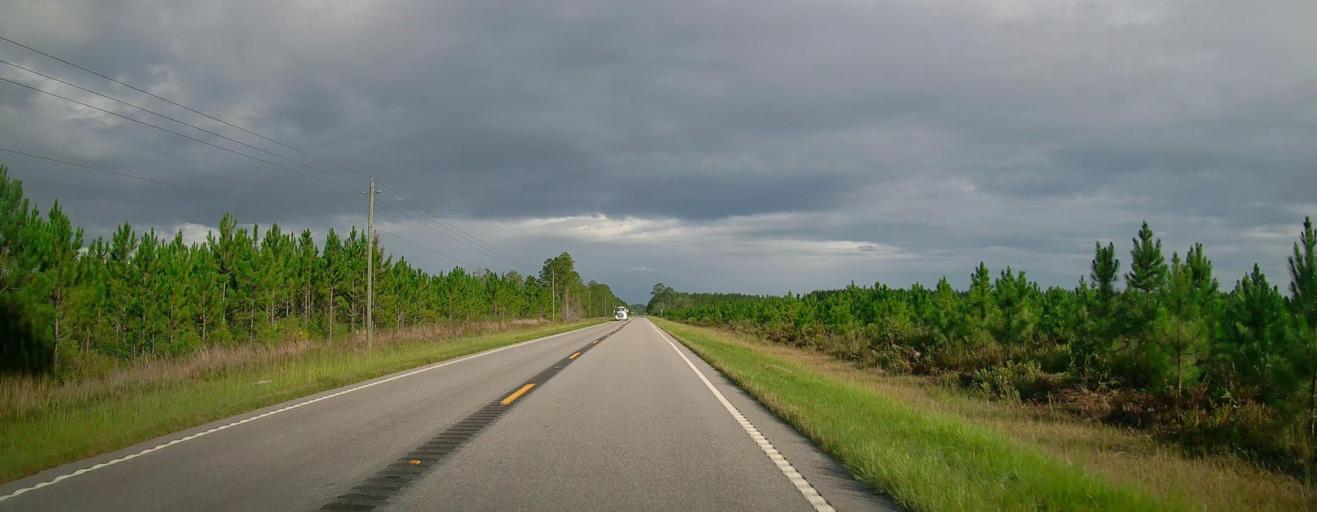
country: US
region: Georgia
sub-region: Coffee County
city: Nicholls
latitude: 31.3708
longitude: -82.6336
